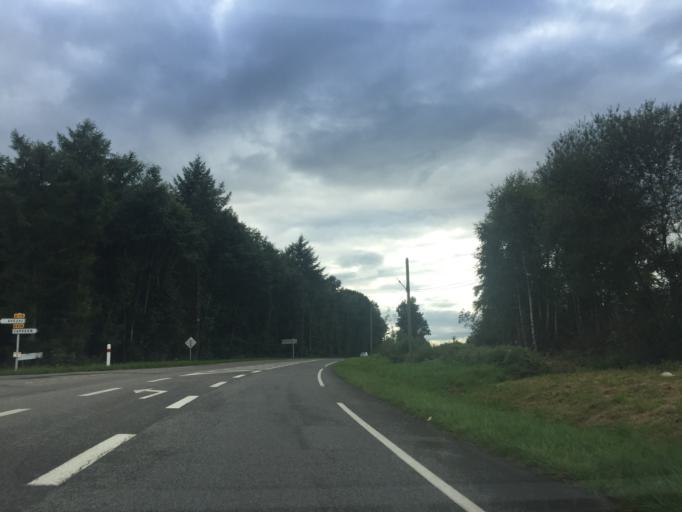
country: FR
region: Midi-Pyrenees
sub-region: Departement des Hautes-Pyrenees
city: La Barthe-de-Neste
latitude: 43.0803
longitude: 0.3546
